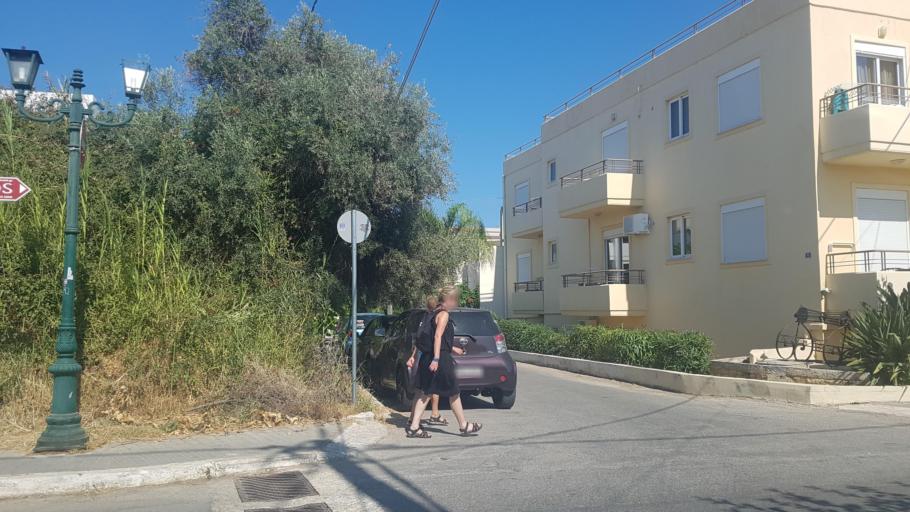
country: GR
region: Crete
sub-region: Nomos Chanias
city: Daratsos
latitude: 35.5103
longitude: 23.9793
